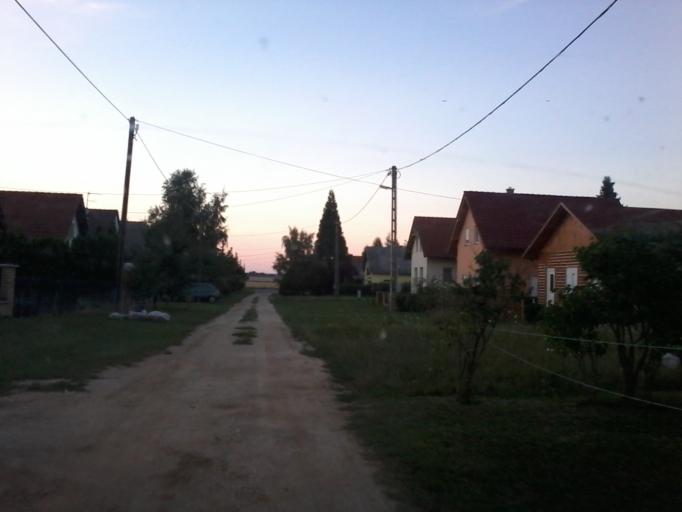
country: HU
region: Vas
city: Janoshaza
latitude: 47.1618
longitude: 17.0951
